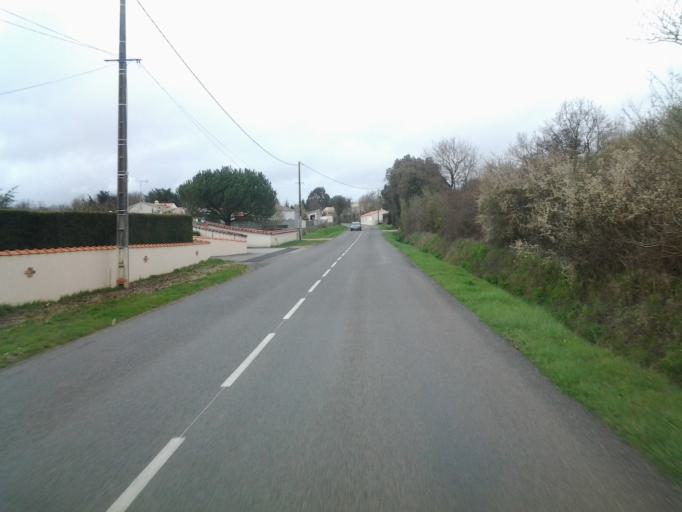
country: FR
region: Pays de la Loire
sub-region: Departement de la Vendee
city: Avrille
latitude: 46.4600
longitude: -1.4863
